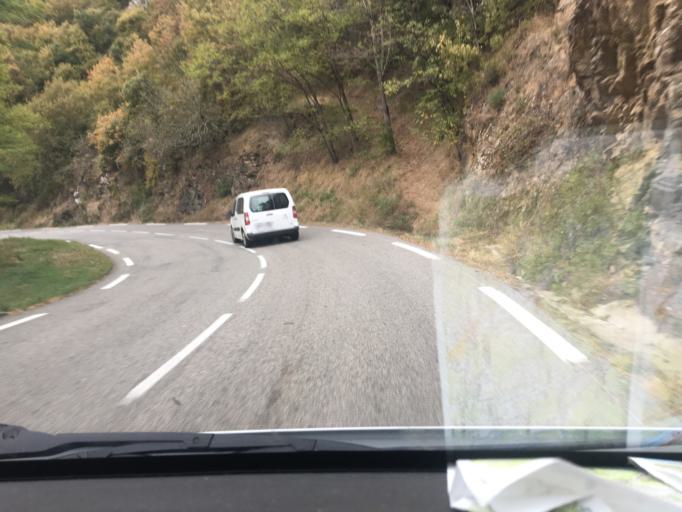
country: FR
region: Rhone-Alpes
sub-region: Departement de l'Ardeche
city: Saint-Jean-de-Muzols
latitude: 45.0645
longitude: 4.7597
